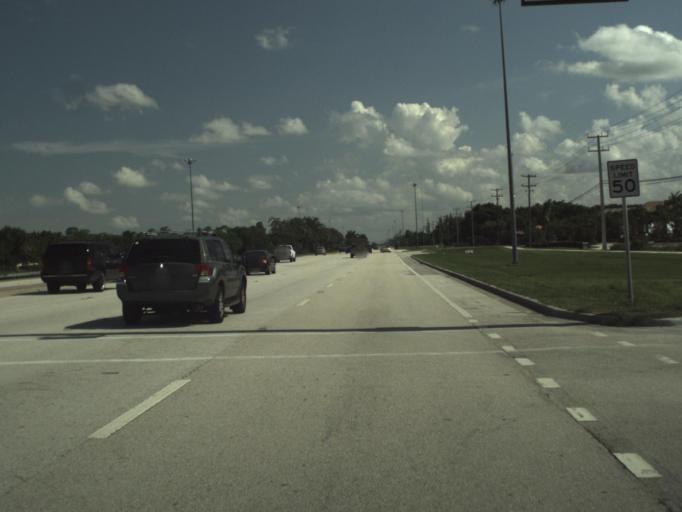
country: US
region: Florida
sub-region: Palm Beach County
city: Wellington
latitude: 26.6283
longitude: -80.2046
